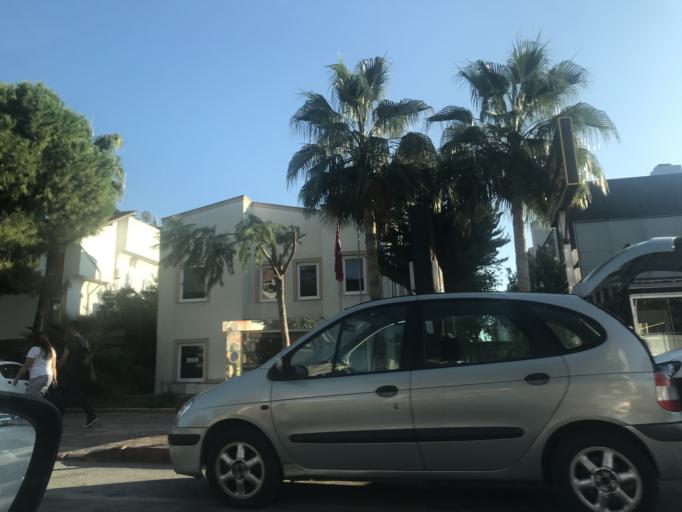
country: TR
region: Antalya
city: Antalya
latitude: 36.8517
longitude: 30.7702
